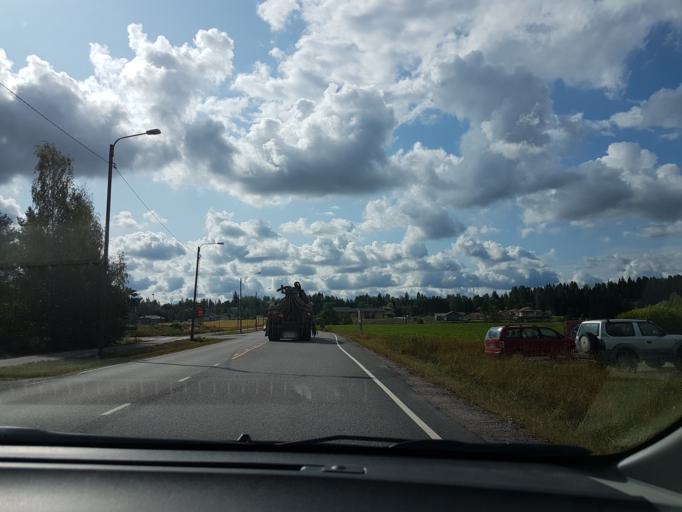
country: FI
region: Uusimaa
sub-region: Helsinki
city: Pornainen
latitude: 60.4844
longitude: 25.3683
